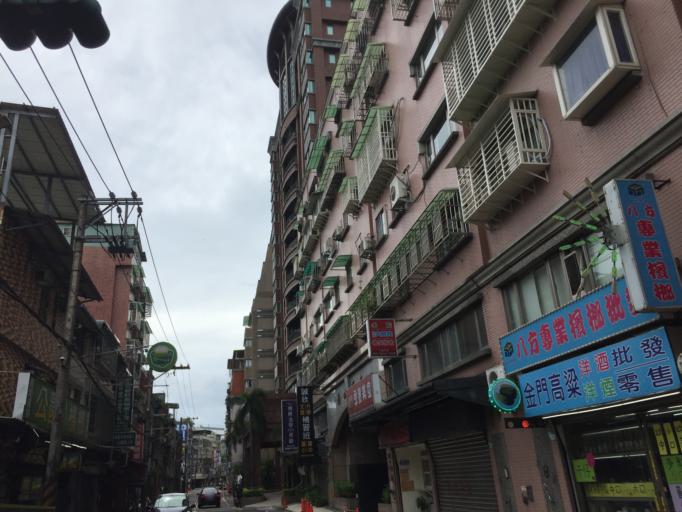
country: TW
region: Taipei
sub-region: Taipei
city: Banqiao
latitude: 24.9912
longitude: 121.5050
